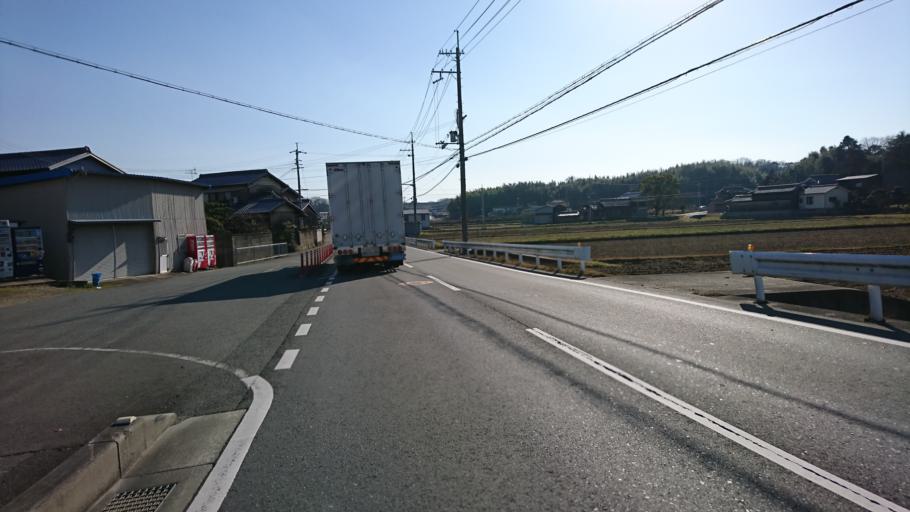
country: JP
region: Hyogo
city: Ono
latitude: 34.7888
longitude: 134.9010
